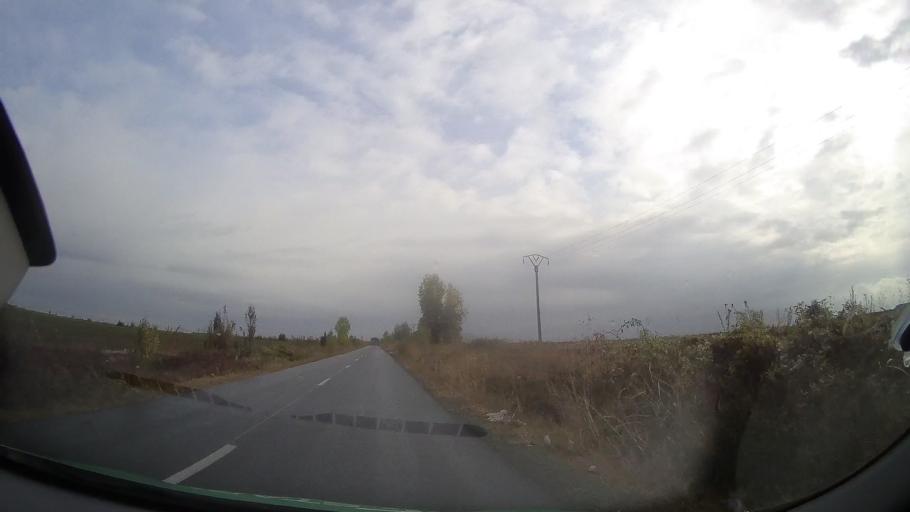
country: RO
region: Ialomita
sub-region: Comuna Maia
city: Maia
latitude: 44.7512
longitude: 26.3896
